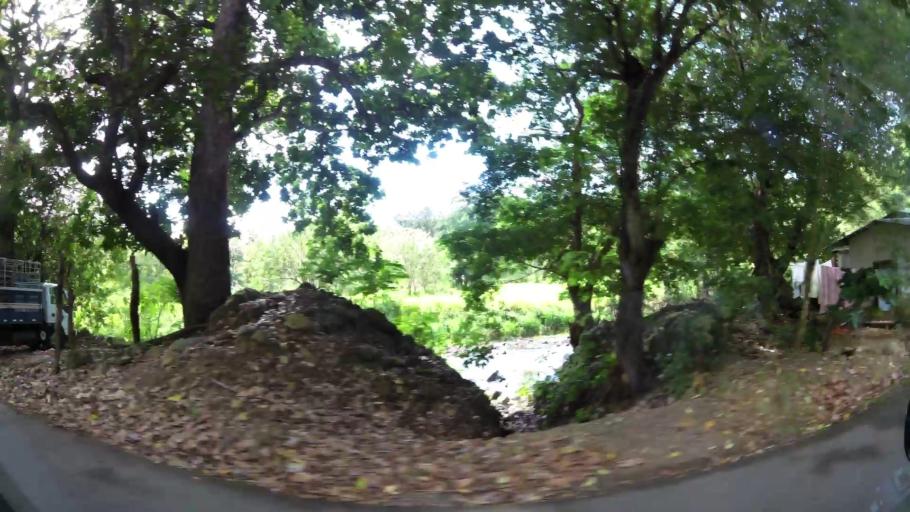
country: CR
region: Guanacaste
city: Juntas
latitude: 10.2813
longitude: -84.9413
